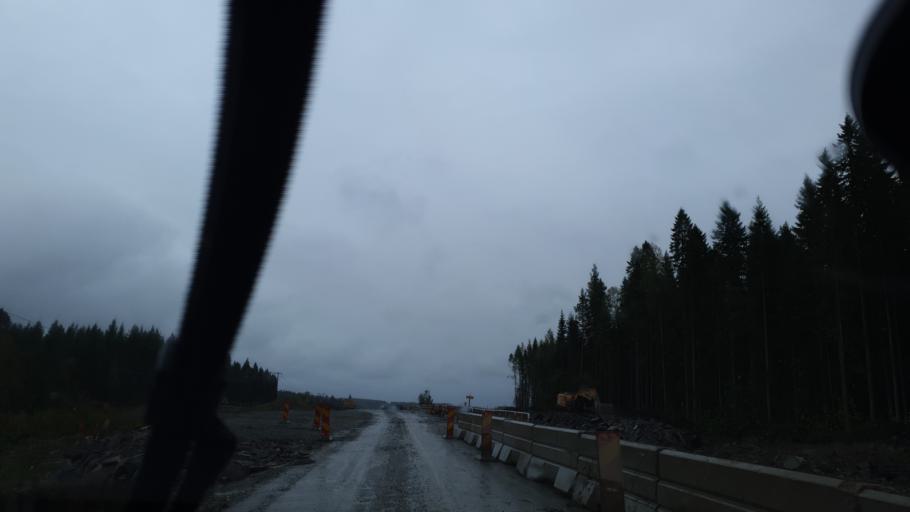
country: SE
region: Vaesterbotten
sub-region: Skelleftea Kommun
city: Soedra Bergsbyn
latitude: 64.7415
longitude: 21.0724
